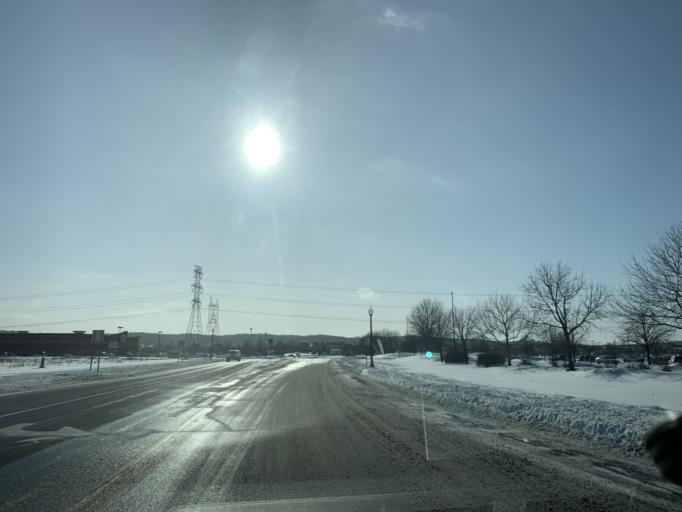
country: US
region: Minnesota
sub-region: Scott County
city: Prior Lake
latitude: 44.7803
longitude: -93.4149
